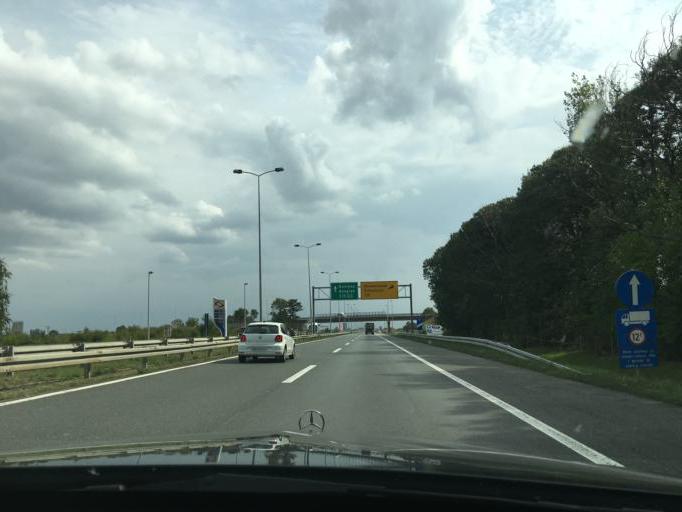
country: RS
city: Simanovci
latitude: 44.8784
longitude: 20.1216
